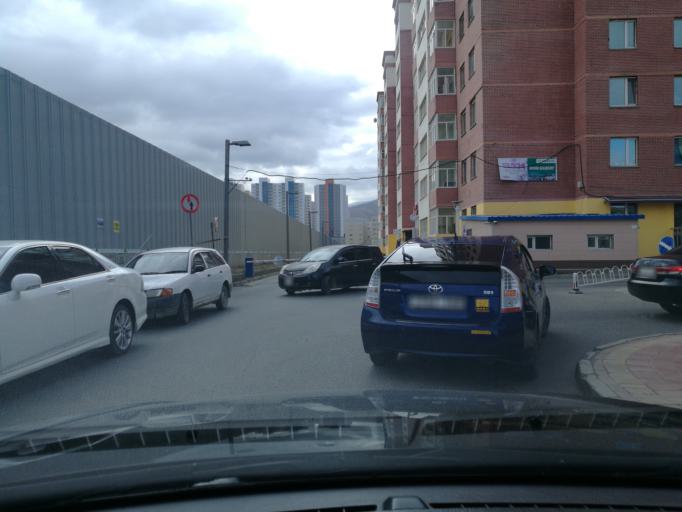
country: MN
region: Ulaanbaatar
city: Ulaanbaatar
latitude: 47.9017
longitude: 106.9207
